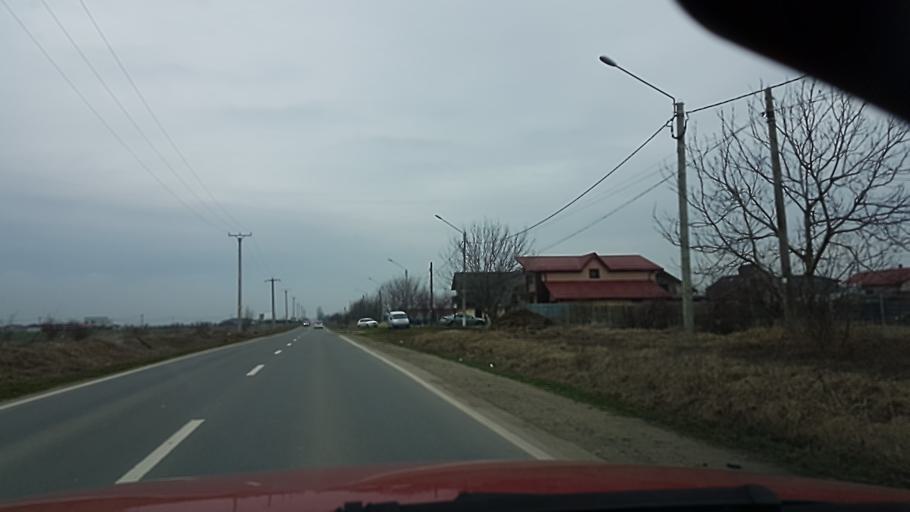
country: RO
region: Ilfov
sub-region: Comuna Balotesti
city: Balotesti
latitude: 44.6192
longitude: 26.1249
